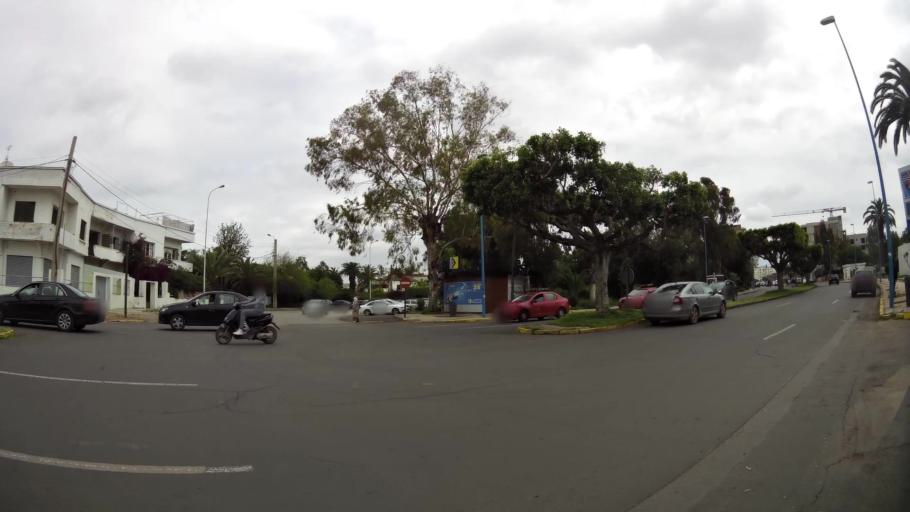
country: MA
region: Grand Casablanca
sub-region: Casablanca
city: Casablanca
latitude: 33.5573
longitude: -7.6354
